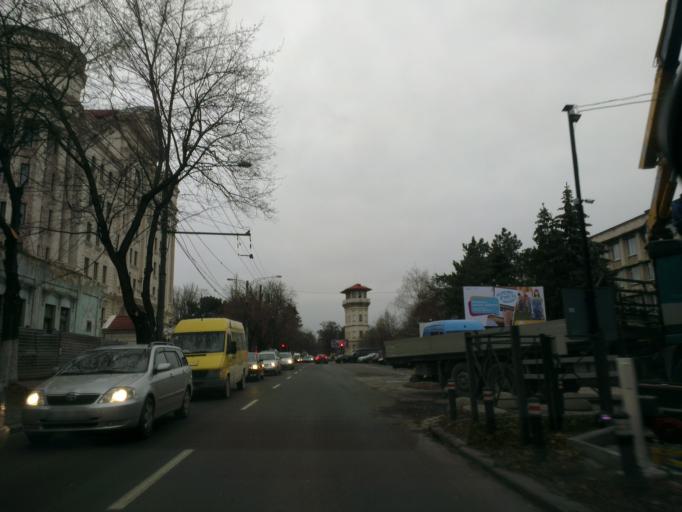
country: MD
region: Chisinau
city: Chisinau
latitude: 47.0177
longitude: 28.8240
